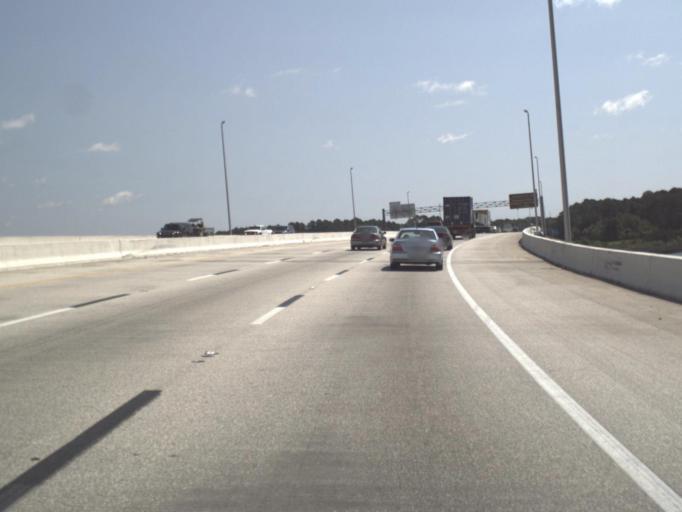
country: US
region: Florida
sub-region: Duval County
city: Jacksonville
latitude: 30.3997
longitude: -81.6664
